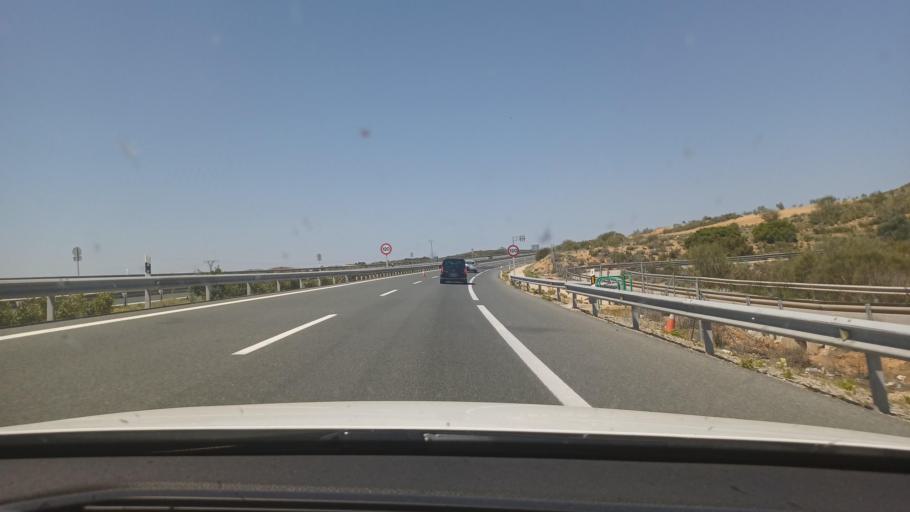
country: ES
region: Castille-La Mancha
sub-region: Provincia de Albacete
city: Almansa
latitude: 38.8757
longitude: -1.1782
